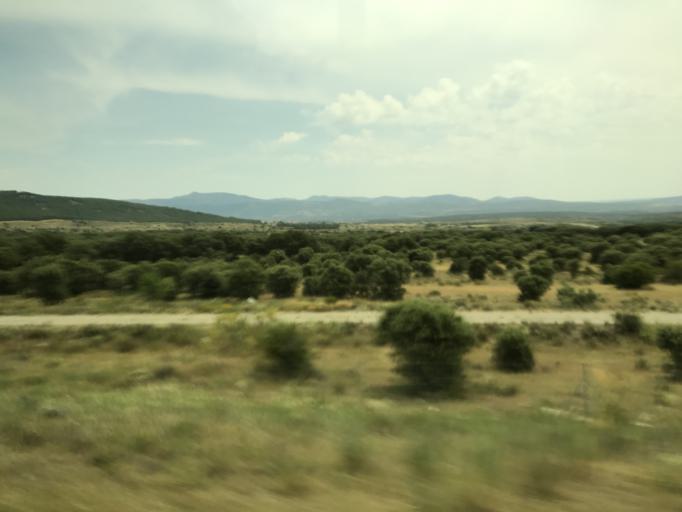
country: ES
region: Madrid
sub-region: Provincia de Madrid
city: Buitrago del Lozoya
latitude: 40.9513
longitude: -3.6393
